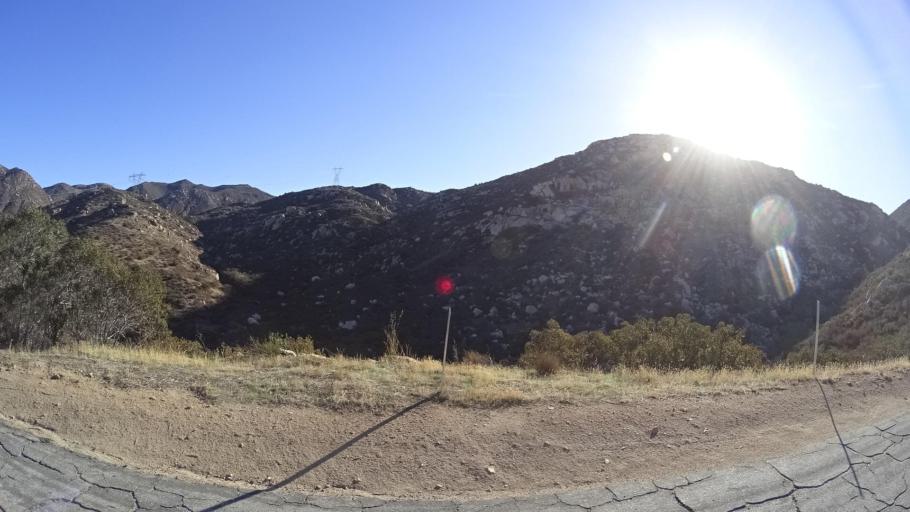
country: MX
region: Baja California
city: Tecate
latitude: 32.6018
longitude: -116.6811
